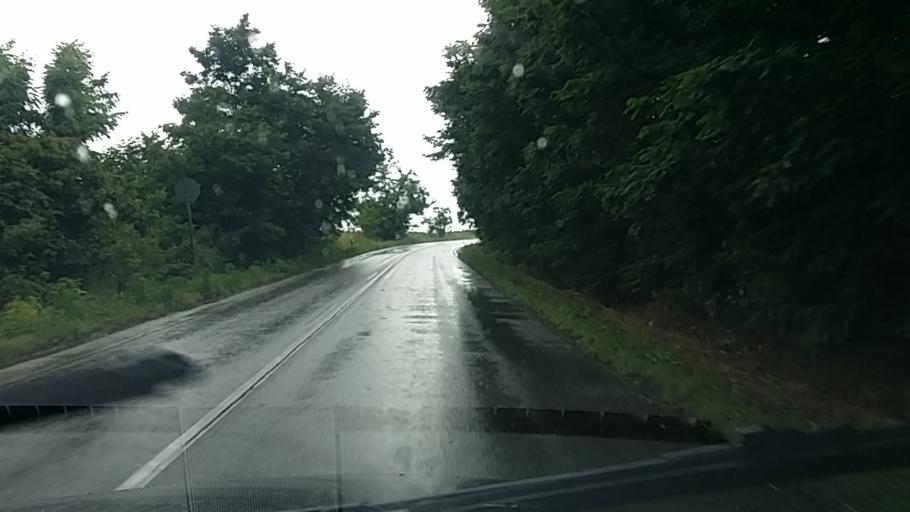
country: HU
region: Pest
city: Felsopakony
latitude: 47.3194
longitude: 19.2947
